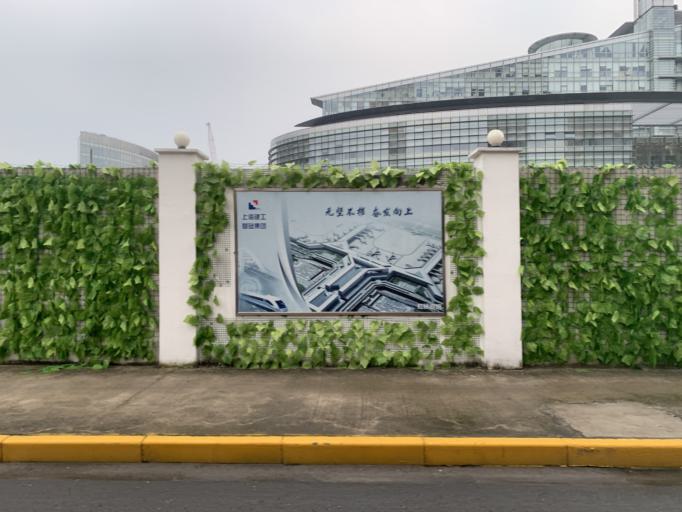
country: CN
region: Shanghai Shi
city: Huamu
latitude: 31.2236
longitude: 121.5469
